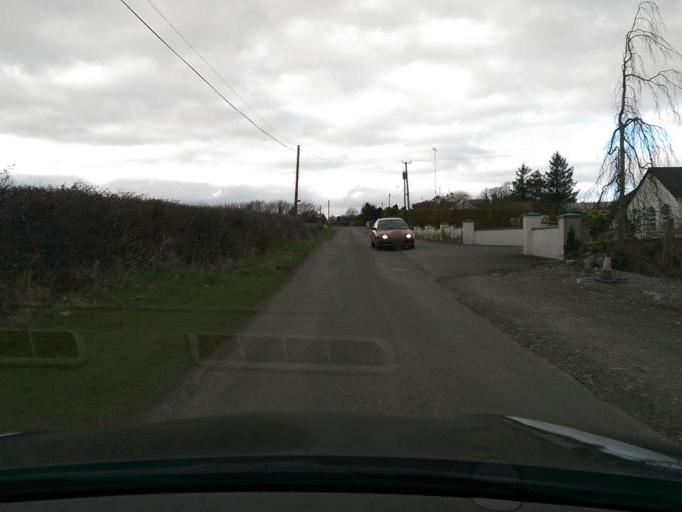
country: IE
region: Leinster
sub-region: Uibh Fhaili
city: Clara
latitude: 53.4030
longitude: -7.6212
